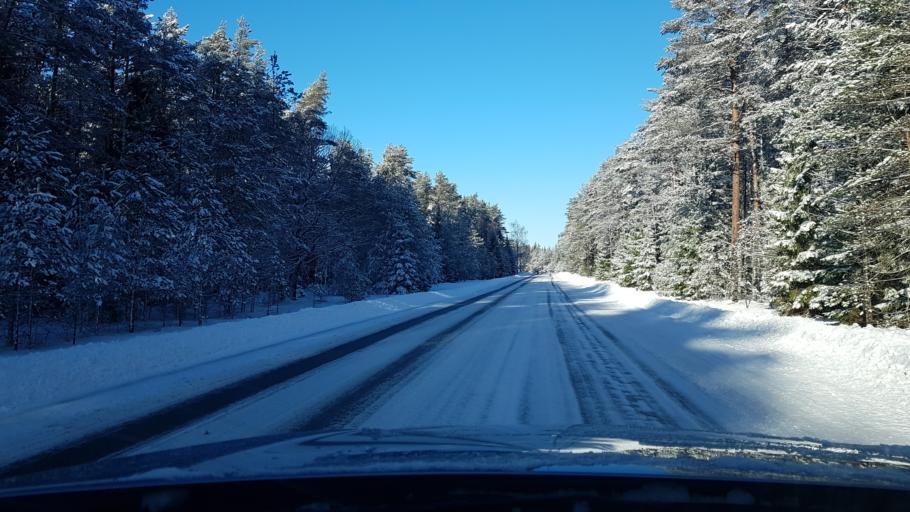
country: EE
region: Hiiumaa
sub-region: Kaerdla linn
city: Kardla
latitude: 58.9329
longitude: 22.7828
